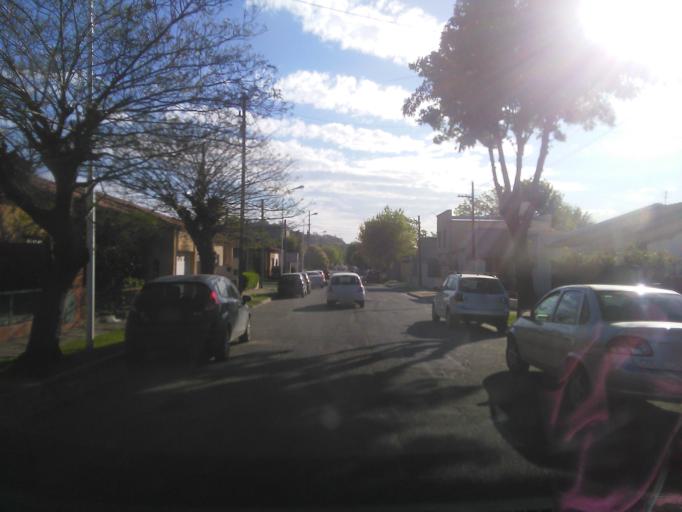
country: AR
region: Buenos Aires
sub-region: Partido de Tandil
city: Tandil
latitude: -37.3334
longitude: -59.1238
